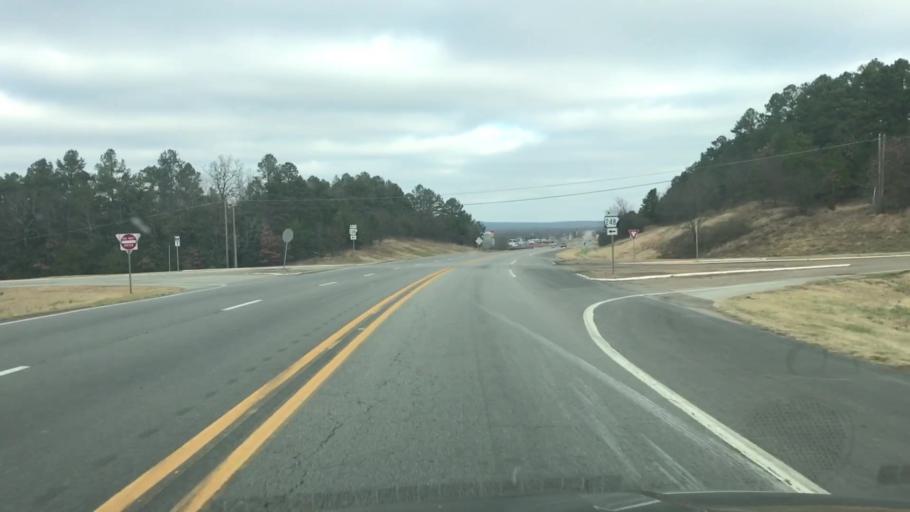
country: US
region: Arkansas
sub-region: Scott County
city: Waldron
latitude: 34.8874
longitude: -94.1076
